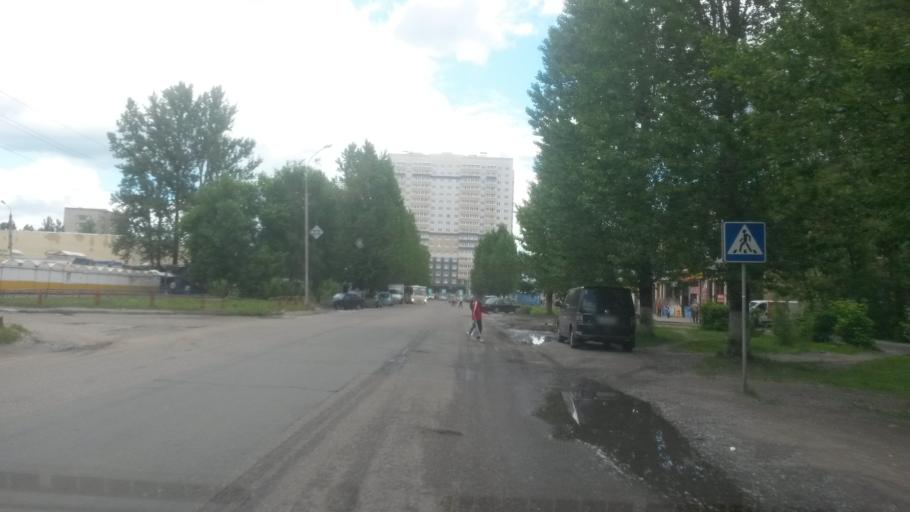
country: RU
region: Jaroslavl
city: Yaroslavl
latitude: 57.6848
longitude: 39.8018
